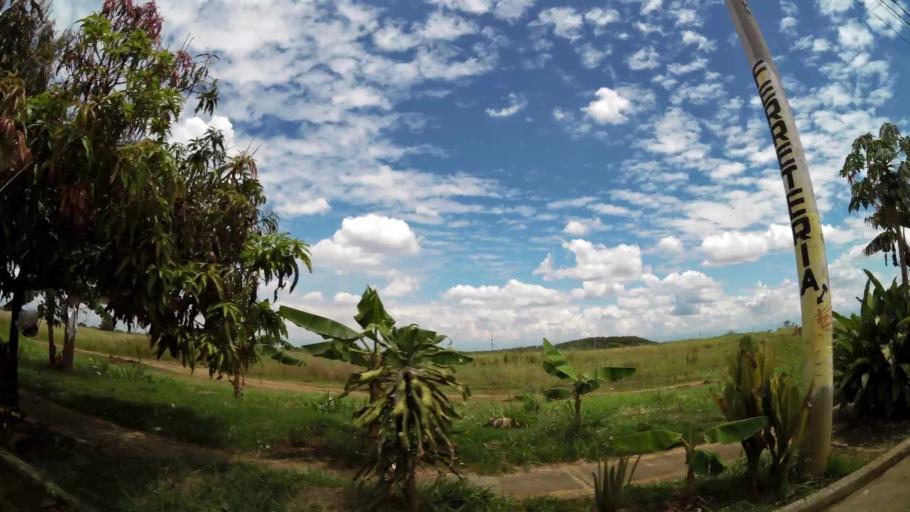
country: CO
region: Valle del Cauca
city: Cali
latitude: 3.3798
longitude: -76.5079
